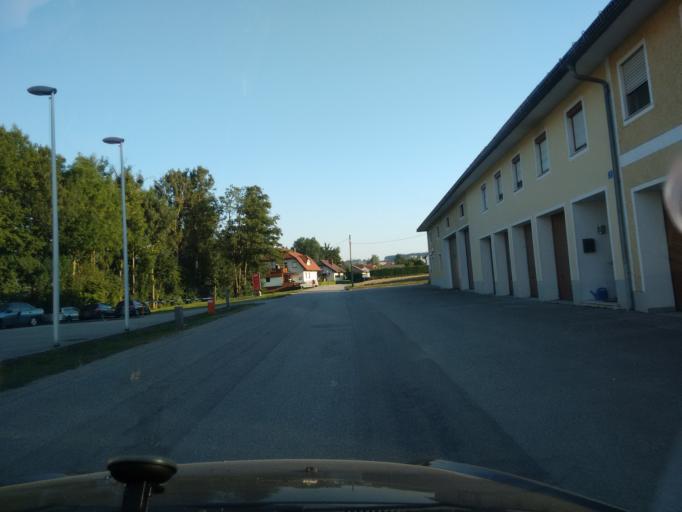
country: AT
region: Upper Austria
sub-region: Politischer Bezirk Grieskirchen
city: Bad Schallerbach
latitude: 48.2090
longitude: 13.9553
